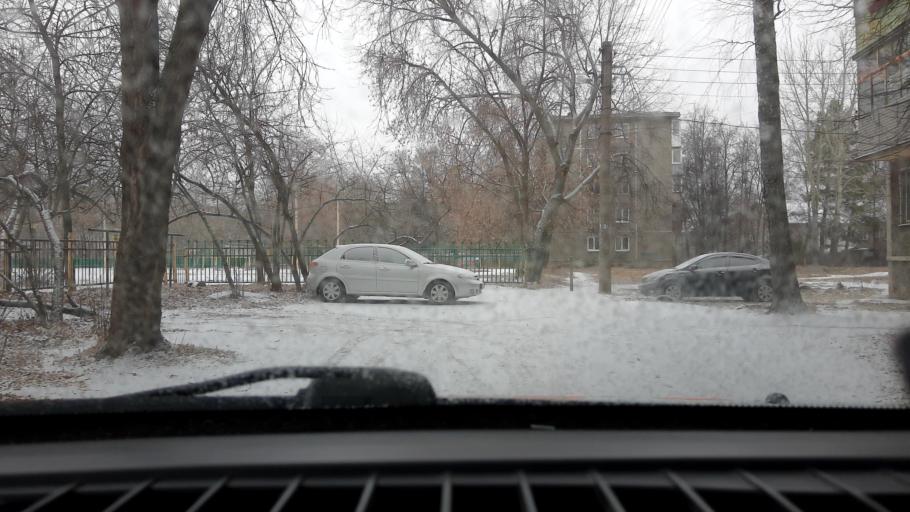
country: RU
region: Nizjnij Novgorod
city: Gorbatovka
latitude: 56.3544
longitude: 43.8378
